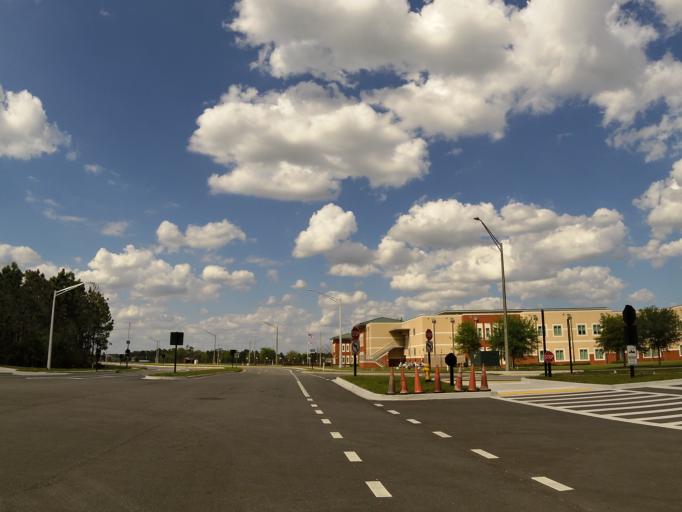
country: US
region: Florida
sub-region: Saint Johns County
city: Palm Valley
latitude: 30.2013
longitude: -81.5070
